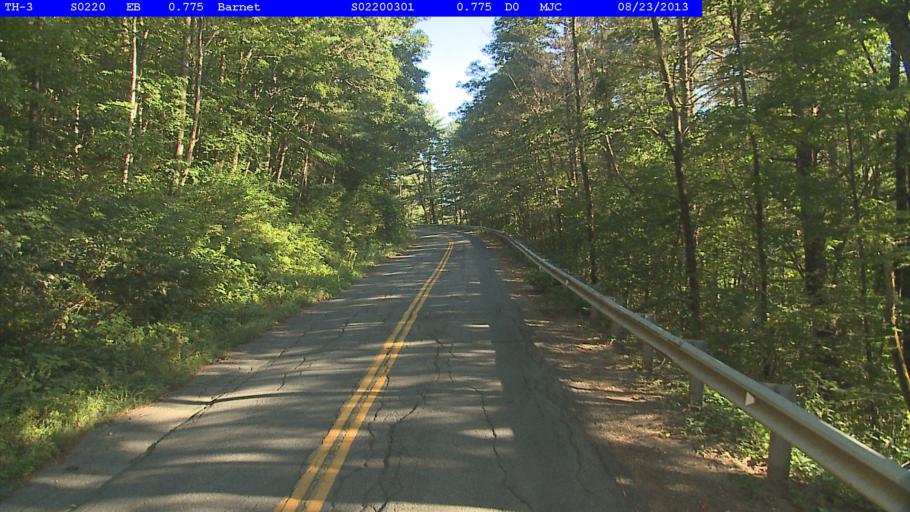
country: US
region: Vermont
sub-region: Caledonia County
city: Saint Johnsbury
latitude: 44.3239
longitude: -72.0330
